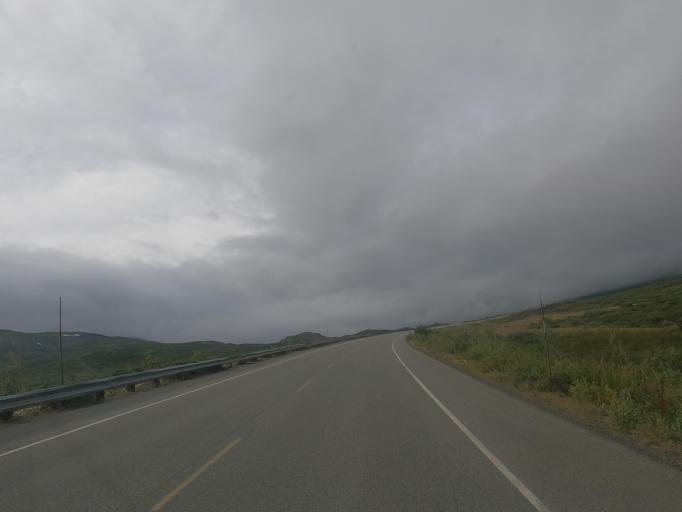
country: US
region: Alaska
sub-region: Haines Borough
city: Haines
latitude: 59.7442
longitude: -136.5867
